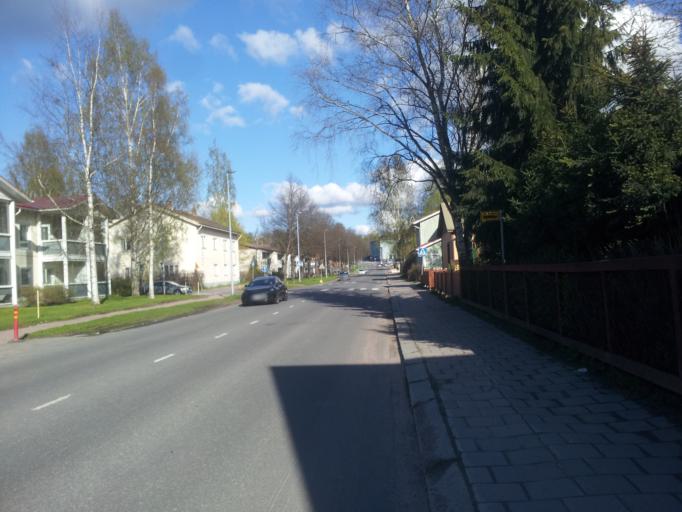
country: FI
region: Haeme
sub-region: Riihimaeki
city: Riihimaeki
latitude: 60.7471
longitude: 24.7735
